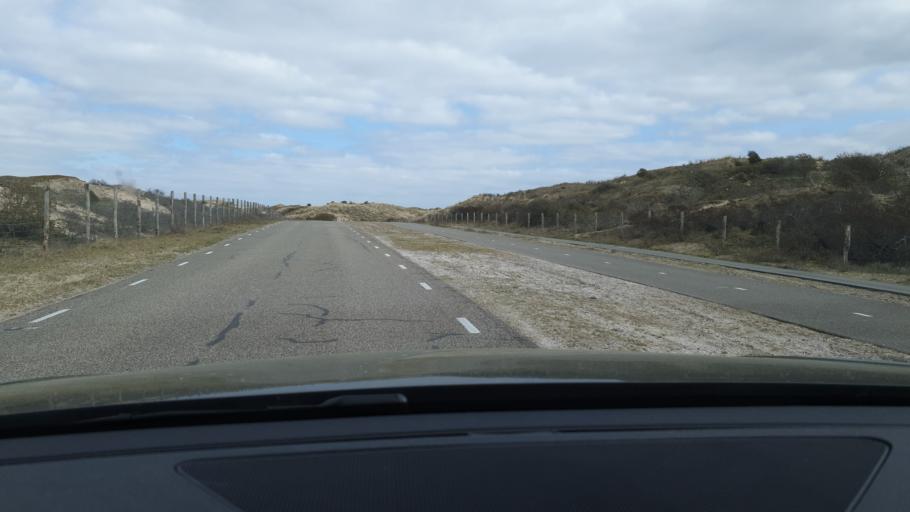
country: NL
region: South Holland
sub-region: Gemeente Noordwijkerhout
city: Noordwijkerhout
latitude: 52.2950
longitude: 4.4833
